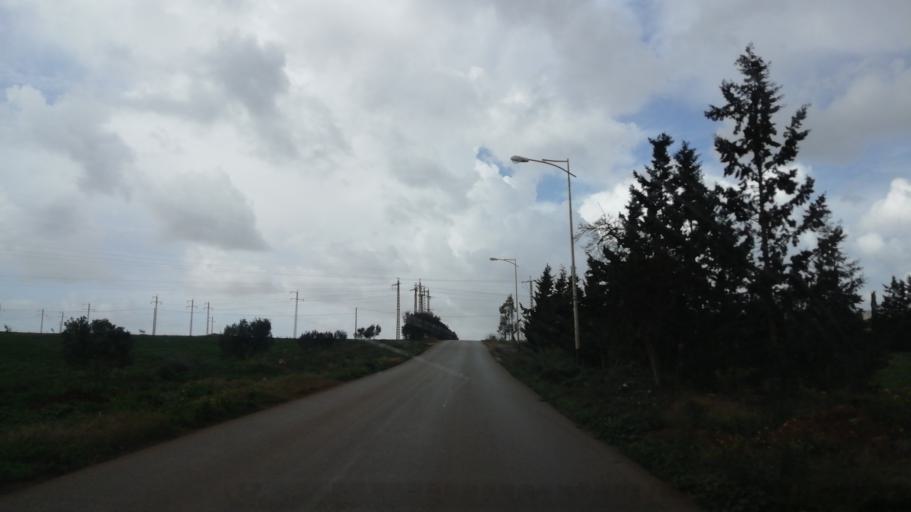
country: DZ
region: Oran
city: Sidi ech Chahmi
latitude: 35.6270
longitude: -0.5320
